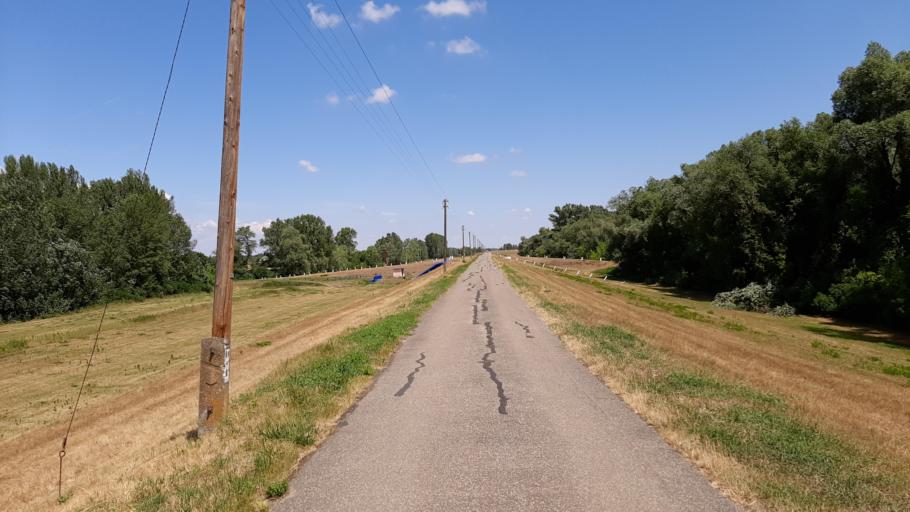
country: HU
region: Csongrad
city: Csanytelek
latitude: 46.5780
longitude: 20.1365
